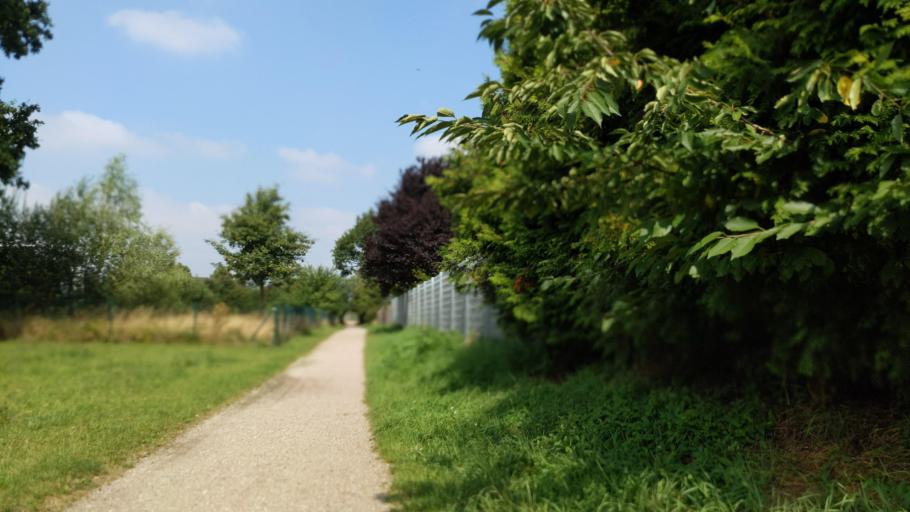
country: DE
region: Schleswig-Holstein
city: Stockelsdorf
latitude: 53.8896
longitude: 10.6314
